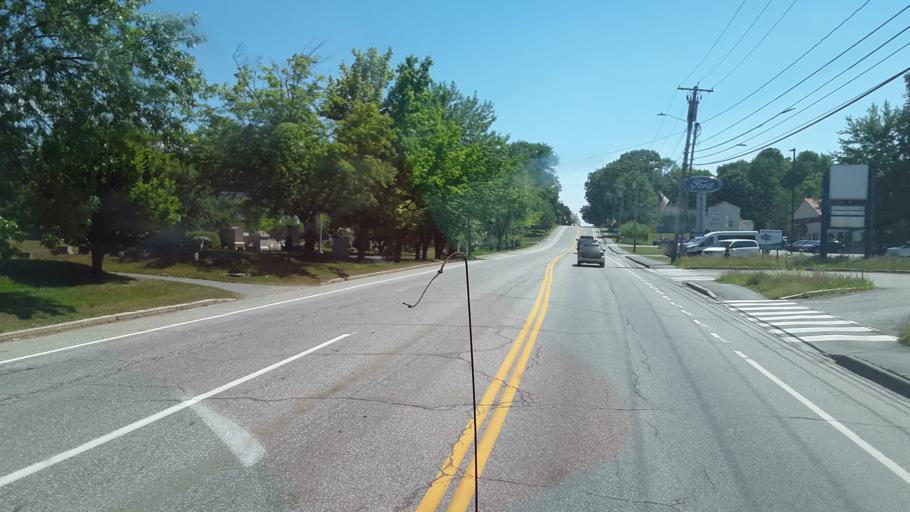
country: US
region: Maine
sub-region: Waldo County
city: Belfast
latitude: 44.4240
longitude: -69.0187
